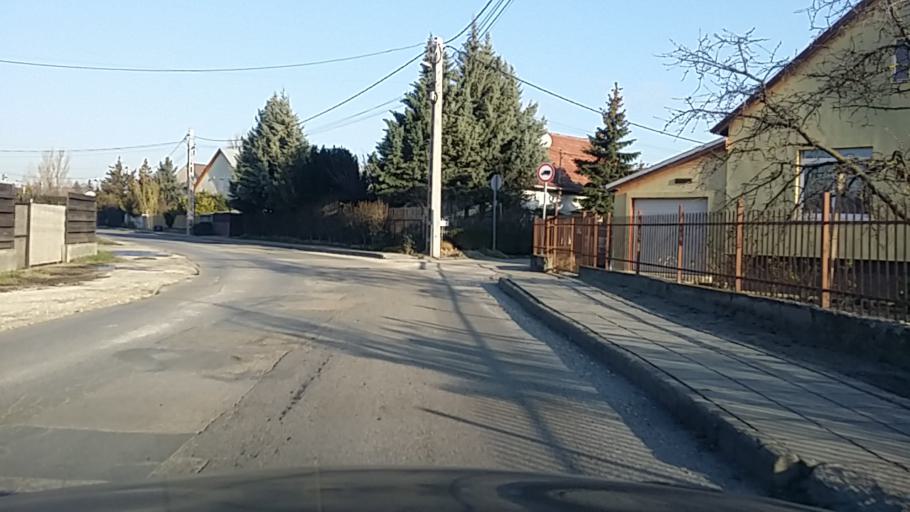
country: HU
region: Pest
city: Szigetszentmiklos
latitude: 47.3439
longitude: 19.0262
